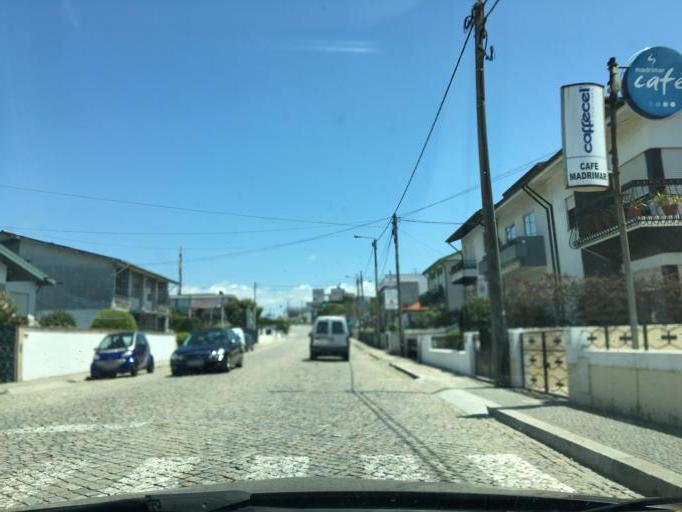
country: PT
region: Porto
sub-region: Maia
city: Gemunde
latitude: 41.2568
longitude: -8.6461
